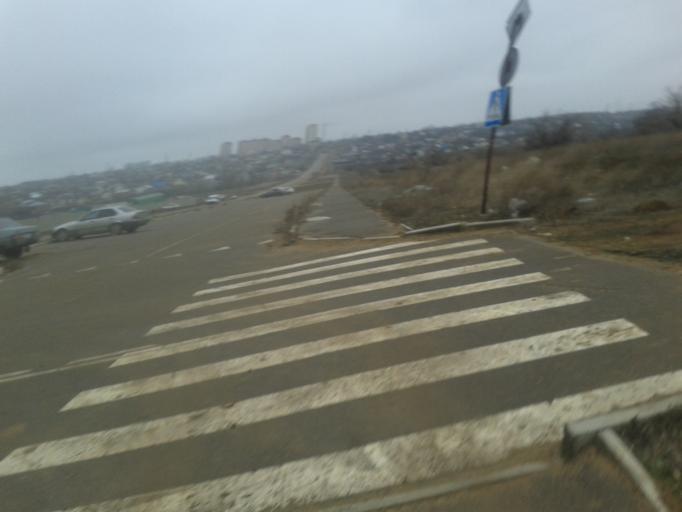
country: RU
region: Volgograd
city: Volgograd
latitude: 48.6603
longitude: 44.4148
